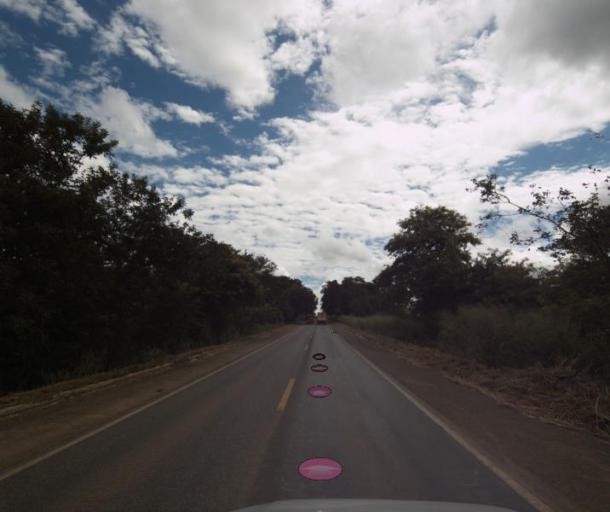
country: BR
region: Goias
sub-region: Uruacu
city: Uruacu
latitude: -14.4146
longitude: -49.1573
